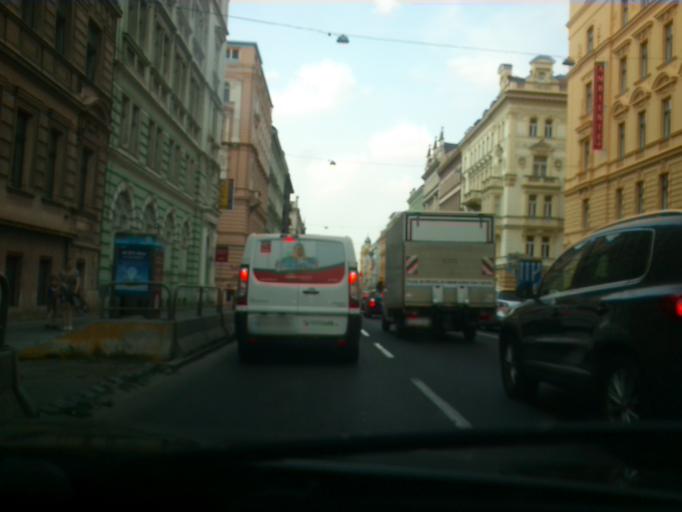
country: CZ
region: Praha
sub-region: Praha 2
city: Vysehrad
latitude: 50.0724
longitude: 14.4305
